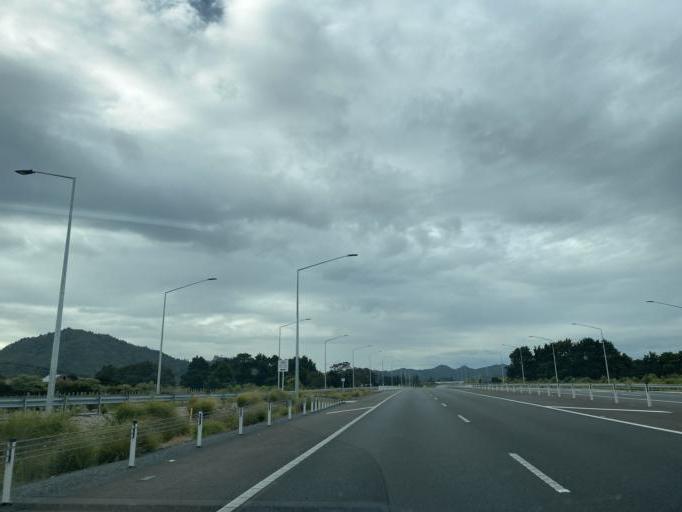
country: NZ
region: Waikato
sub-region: Waikato District
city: Ngaruawahia
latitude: -37.6207
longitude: 175.2054
